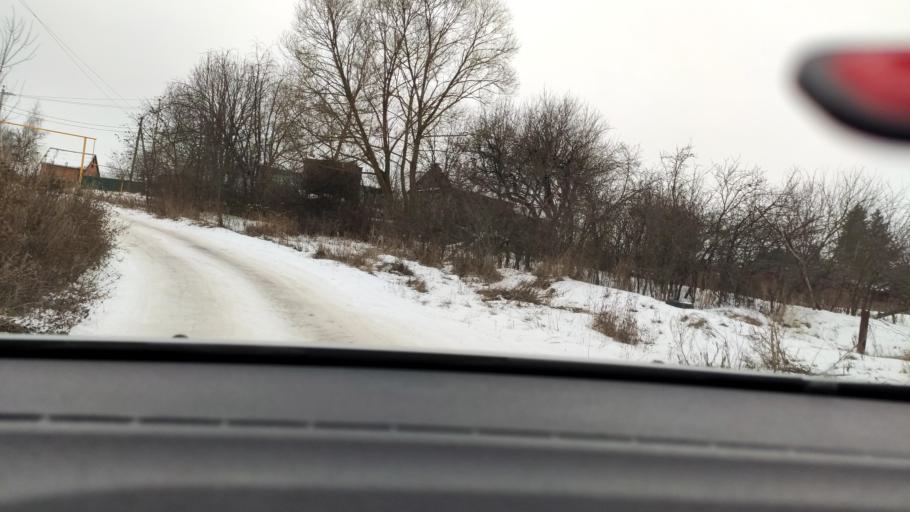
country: RU
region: Voronezj
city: Semiluki
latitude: 51.6990
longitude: 38.9954
